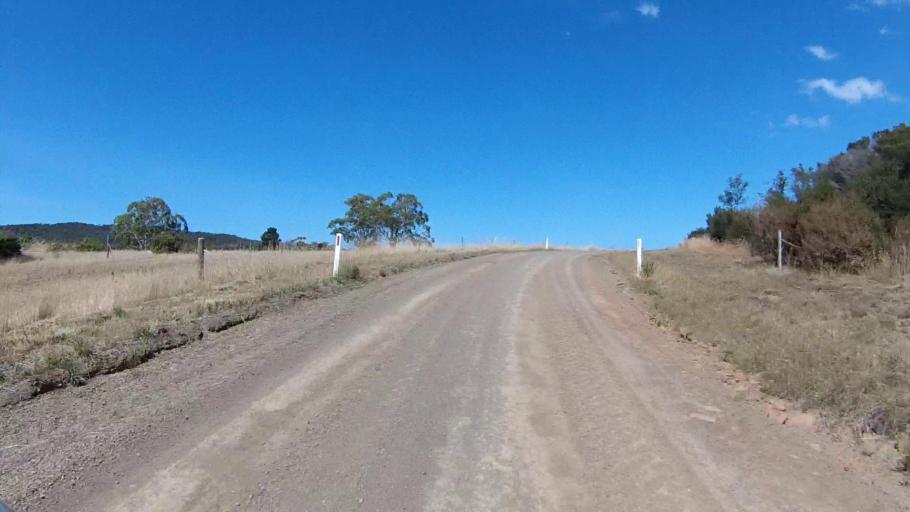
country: AU
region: Tasmania
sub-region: Break O'Day
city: St Helens
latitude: -41.9670
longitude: 148.0745
